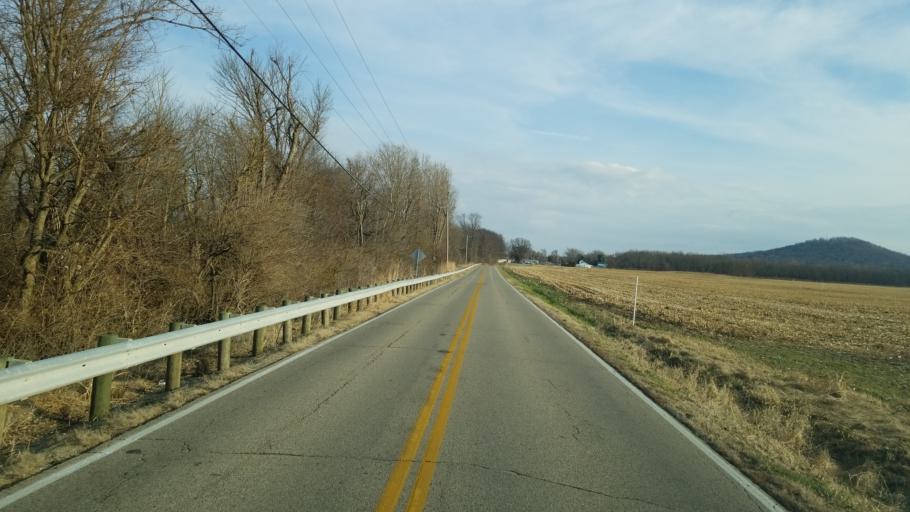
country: US
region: Ohio
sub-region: Ross County
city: Chillicothe
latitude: 39.3880
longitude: -82.9621
